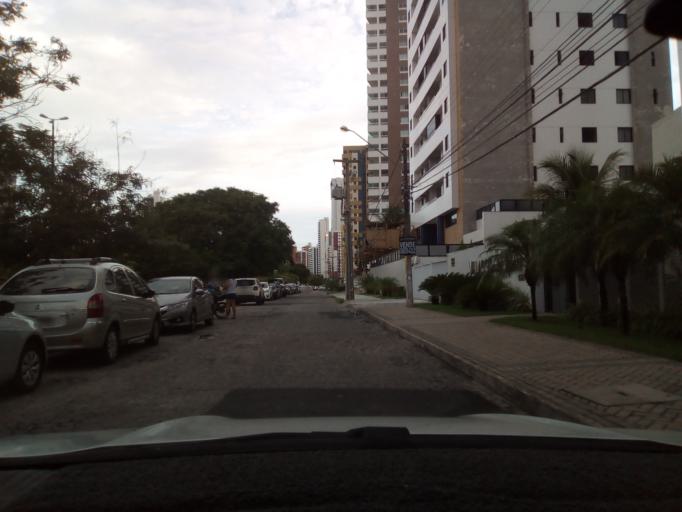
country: BR
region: Paraiba
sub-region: Joao Pessoa
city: Joao Pessoa
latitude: -7.1017
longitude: -34.8389
